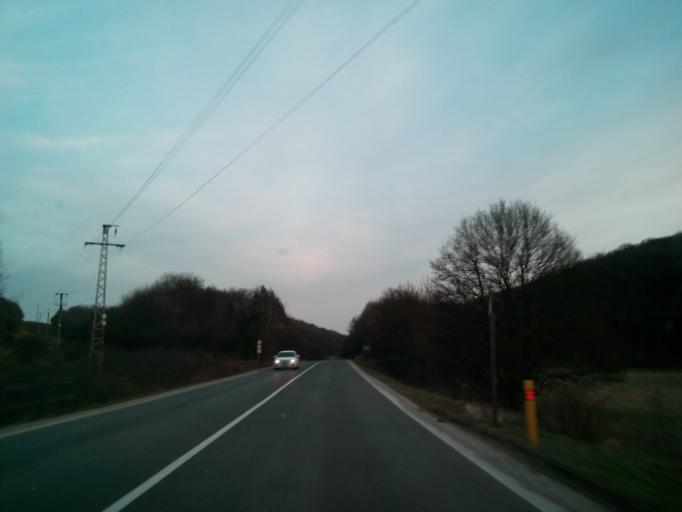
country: SK
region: Kosicky
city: Roznava
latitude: 48.6122
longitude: 20.6352
